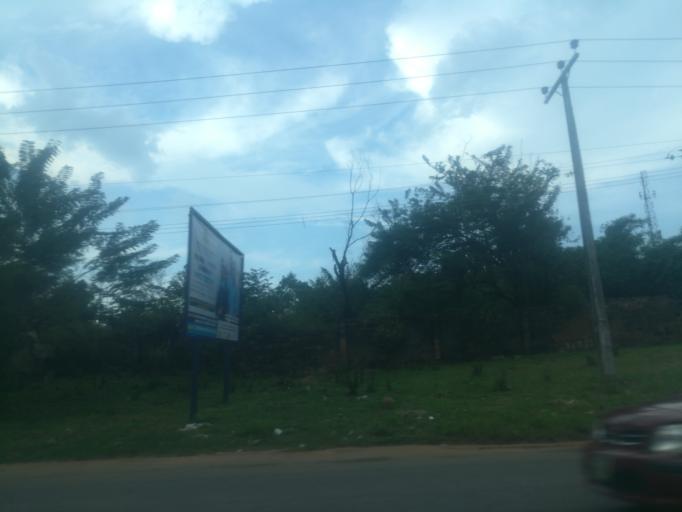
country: NG
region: Oyo
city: Ibadan
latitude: 7.4274
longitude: 3.8903
